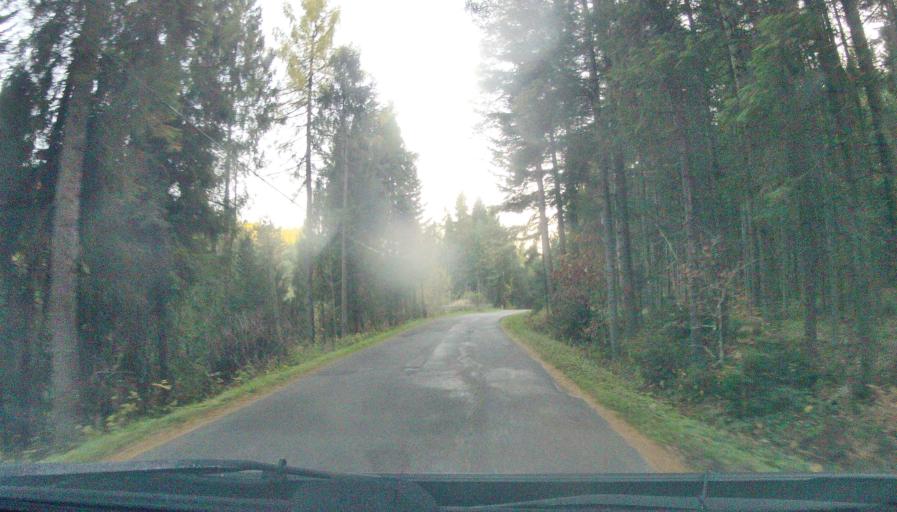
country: PL
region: Lesser Poland Voivodeship
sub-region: Powiat suski
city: Krzeszow
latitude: 49.7590
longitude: 19.4591
